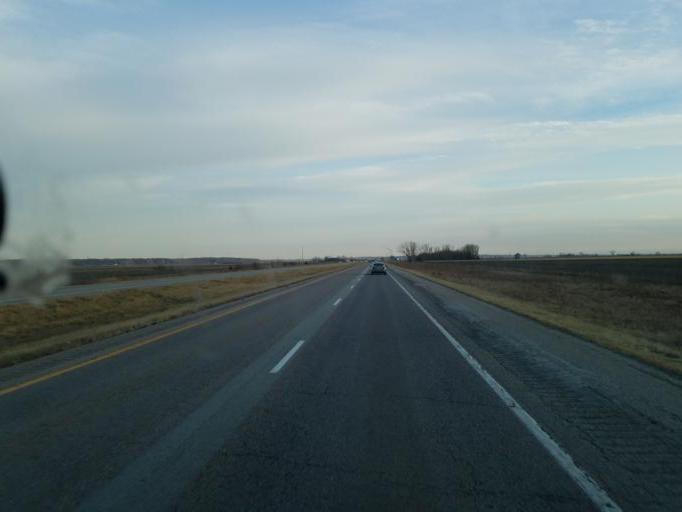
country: US
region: Iowa
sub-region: Harrison County
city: Missouri Valley
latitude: 41.5975
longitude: -95.9592
